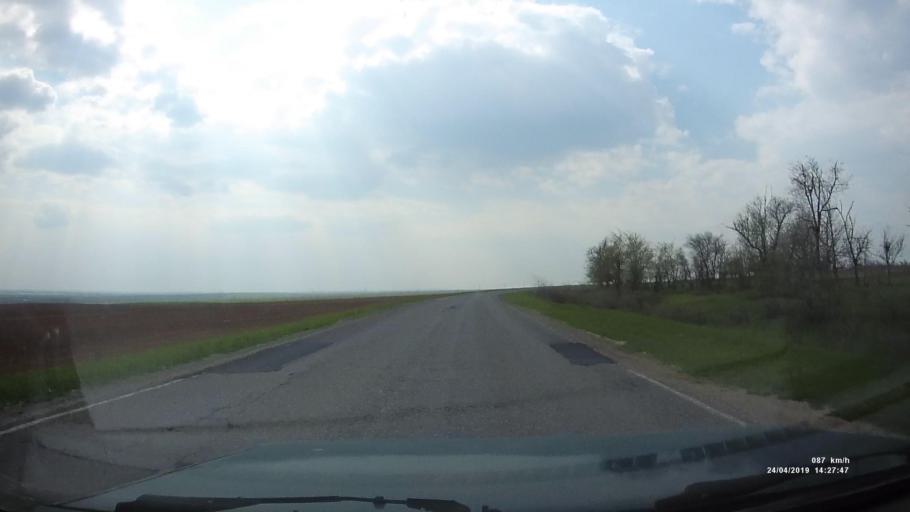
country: RU
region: Kalmykiya
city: Arshan'
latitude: 46.3338
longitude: 44.0361
